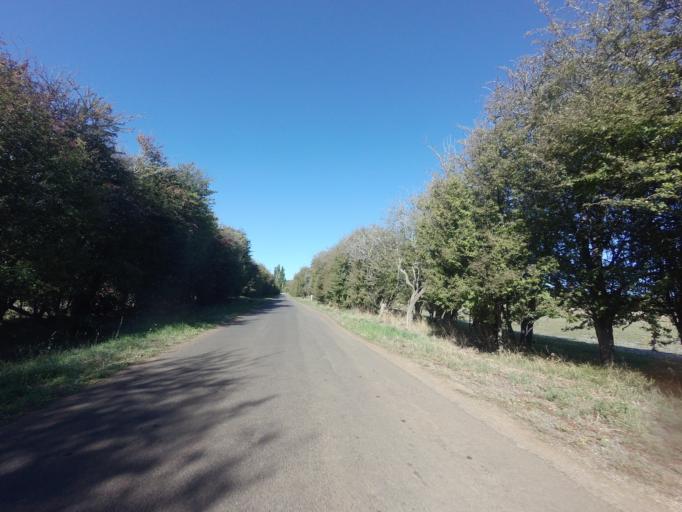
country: AU
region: Tasmania
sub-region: Break O'Day
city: St Helens
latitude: -42.0057
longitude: 148.0721
